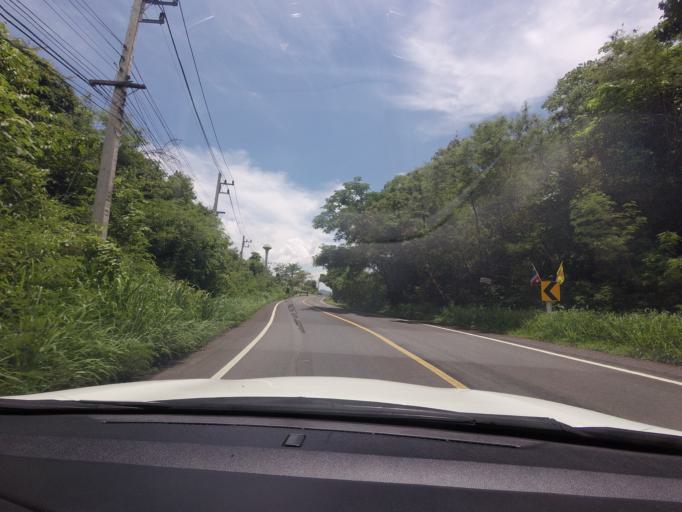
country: TH
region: Sara Buri
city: Muak Lek
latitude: 14.5754
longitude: 101.2764
